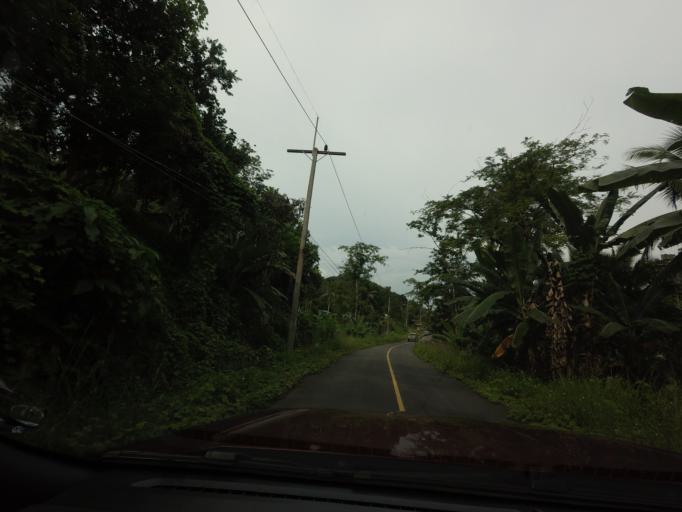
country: TH
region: Narathiwat
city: Si Sakhon
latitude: 6.0610
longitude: 101.3931
